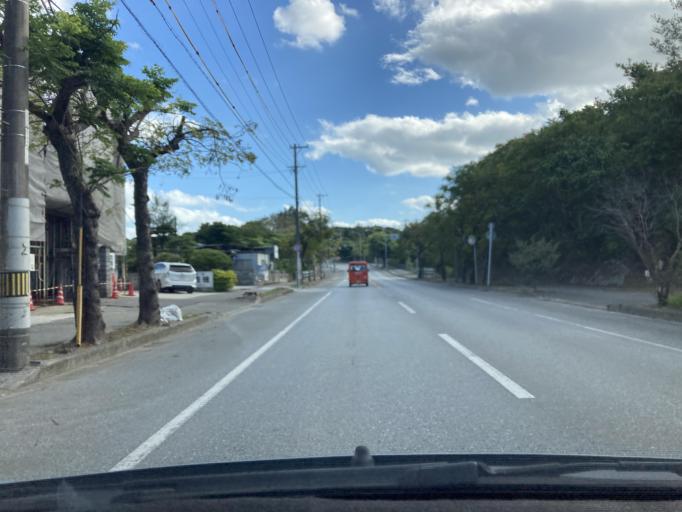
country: JP
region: Okinawa
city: Gushikawa
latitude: 26.3706
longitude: 127.8296
